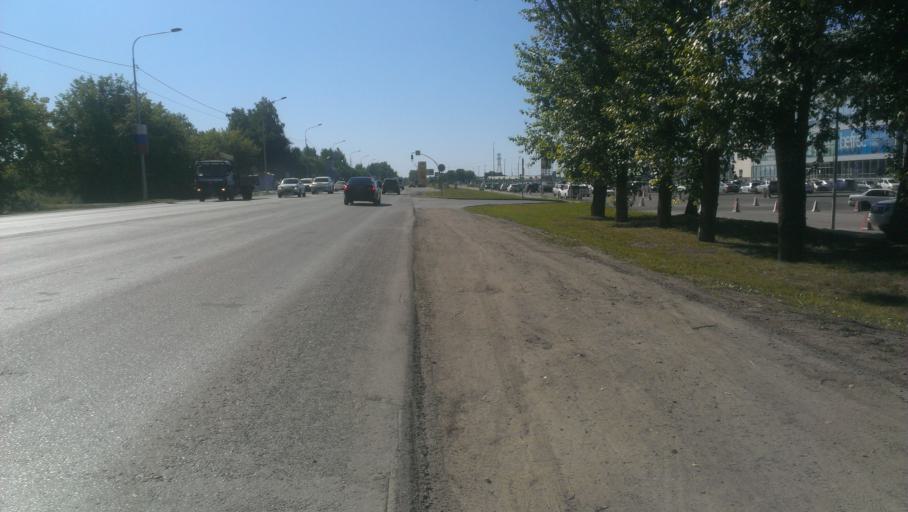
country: RU
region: Altai Krai
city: Novosilikatnyy
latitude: 53.3475
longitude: 83.6402
